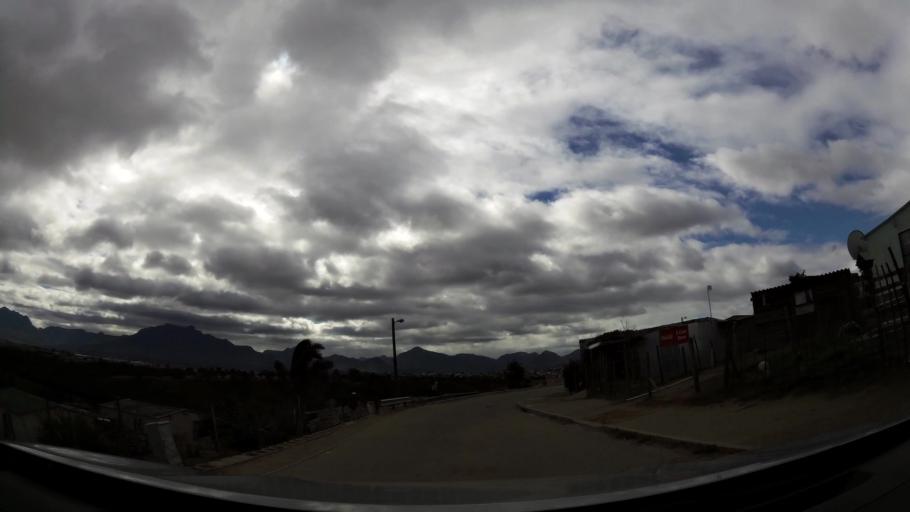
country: ZA
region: Western Cape
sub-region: Eden District Municipality
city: George
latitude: -34.0163
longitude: 22.4687
